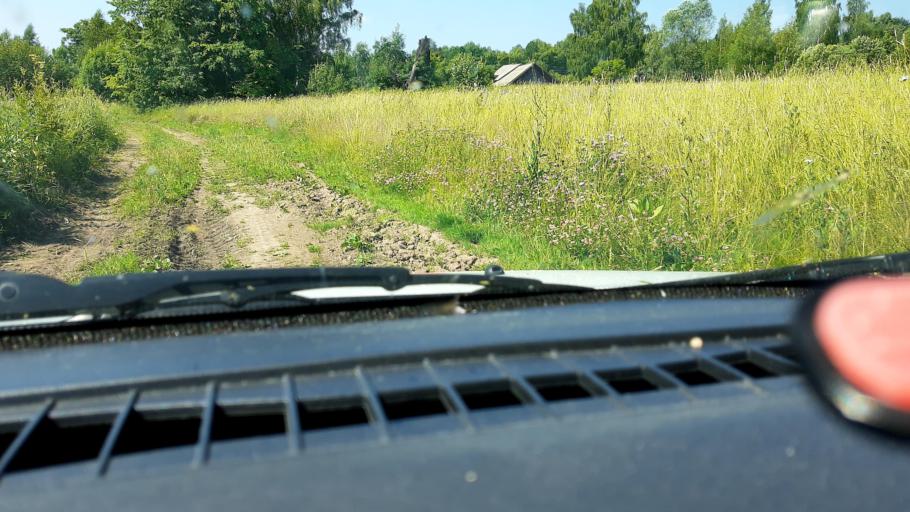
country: RU
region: Nizjnij Novgorod
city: Sharanga
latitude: 57.0417
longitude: 46.7203
